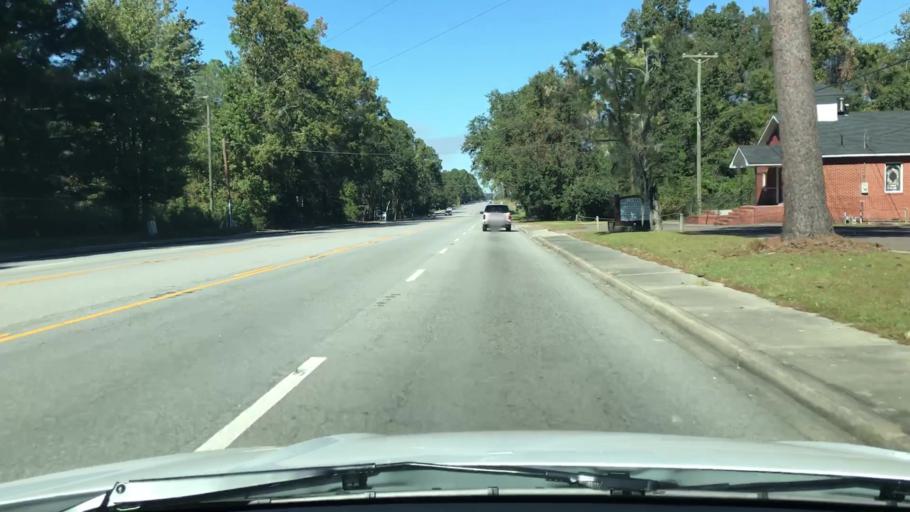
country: US
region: South Carolina
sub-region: Beaufort County
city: Laurel Bay
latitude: 32.5561
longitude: -80.7438
